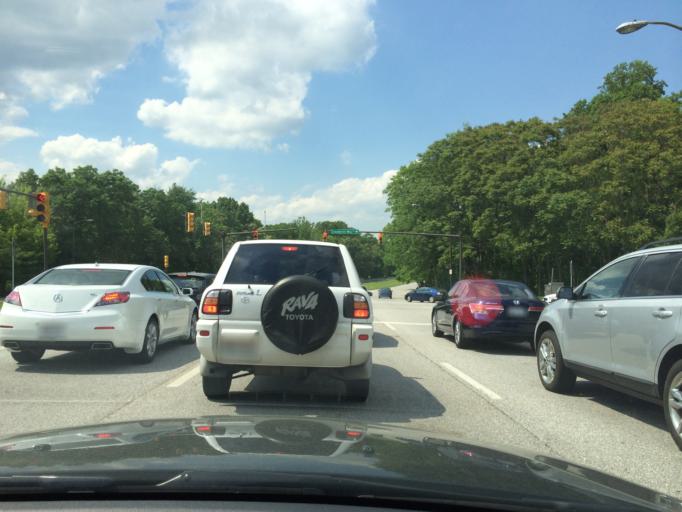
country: US
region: Maryland
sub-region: Howard County
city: Riverside
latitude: 39.1850
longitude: -76.8502
